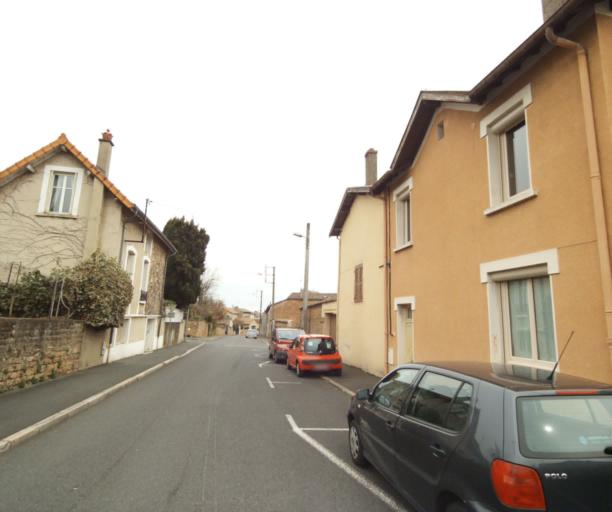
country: FR
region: Bourgogne
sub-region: Departement de Saone-et-Loire
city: Macon
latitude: 46.3050
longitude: 4.8203
